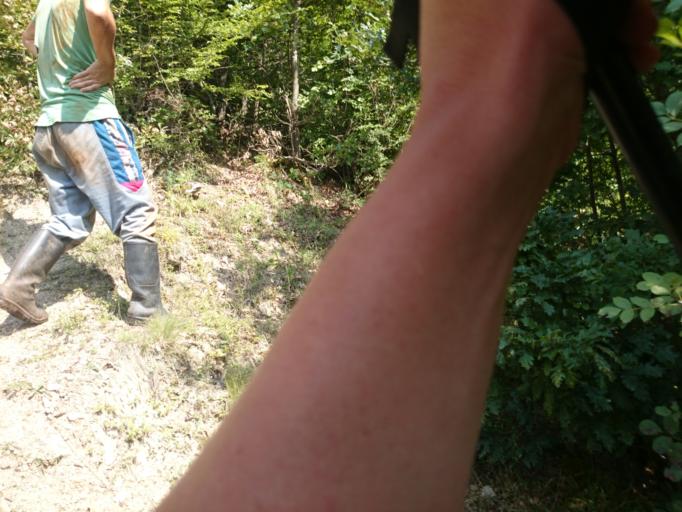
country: AL
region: Diber
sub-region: Rrethi i Dibres
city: Arras
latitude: 41.7421
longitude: 20.2851
